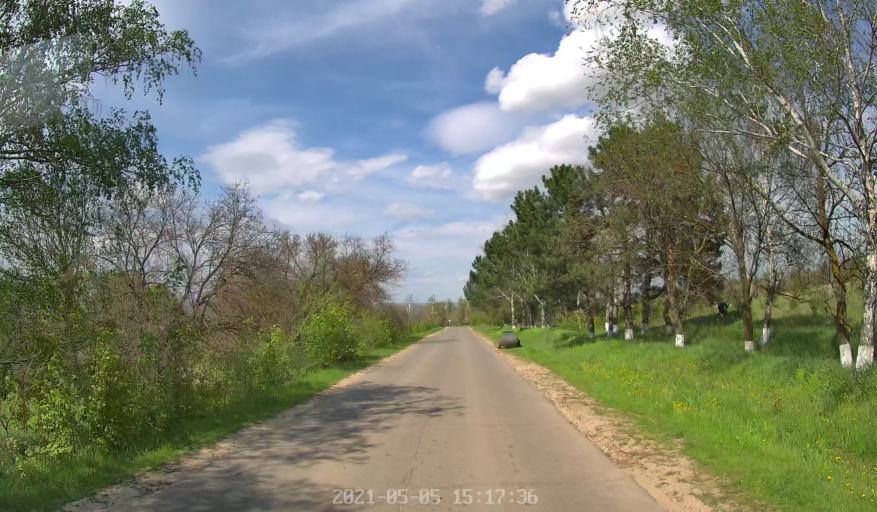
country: MD
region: Criuleni
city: Criuleni
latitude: 47.1131
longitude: 29.1942
